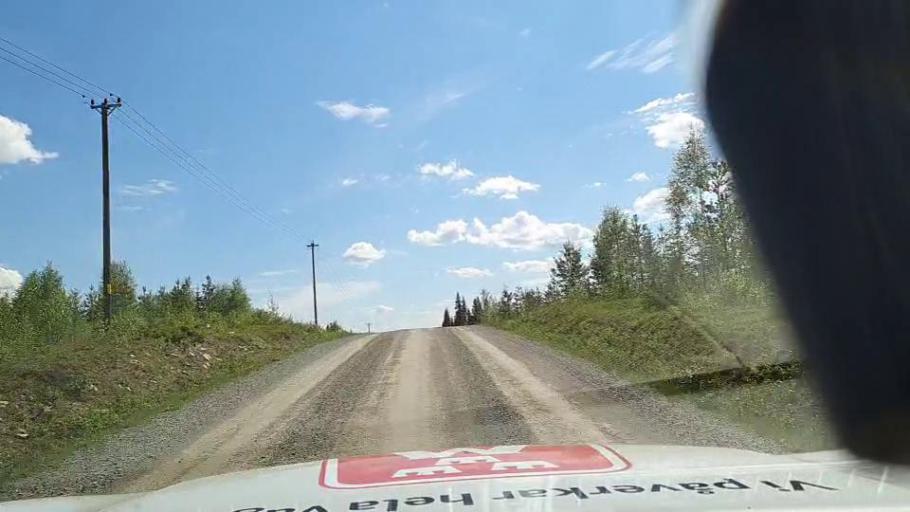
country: SE
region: Jaemtland
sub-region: Stroemsunds Kommun
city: Stroemsund
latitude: 64.4867
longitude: 15.5914
